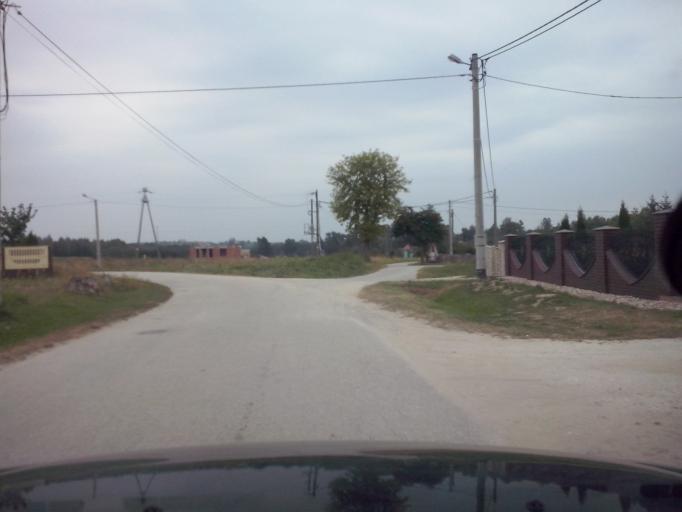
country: PL
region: Swietokrzyskie
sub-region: Powiat kielecki
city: Morawica
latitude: 50.6920
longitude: 20.5755
